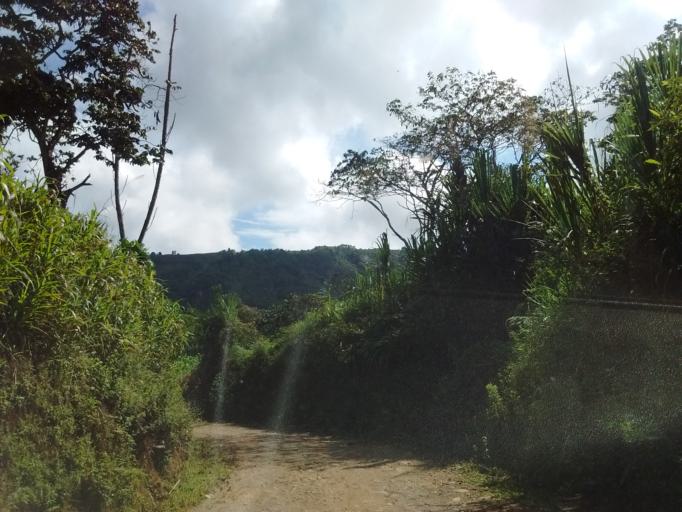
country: CO
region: Cauca
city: Morales
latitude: 2.6908
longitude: -76.7417
